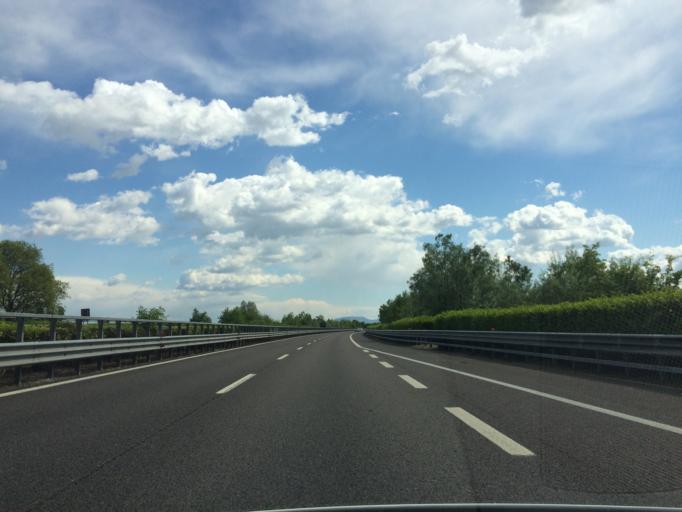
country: IT
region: Veneto
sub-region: Provincia di Vicenza
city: Lisiera
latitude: 45.5632
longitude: 11.6139
